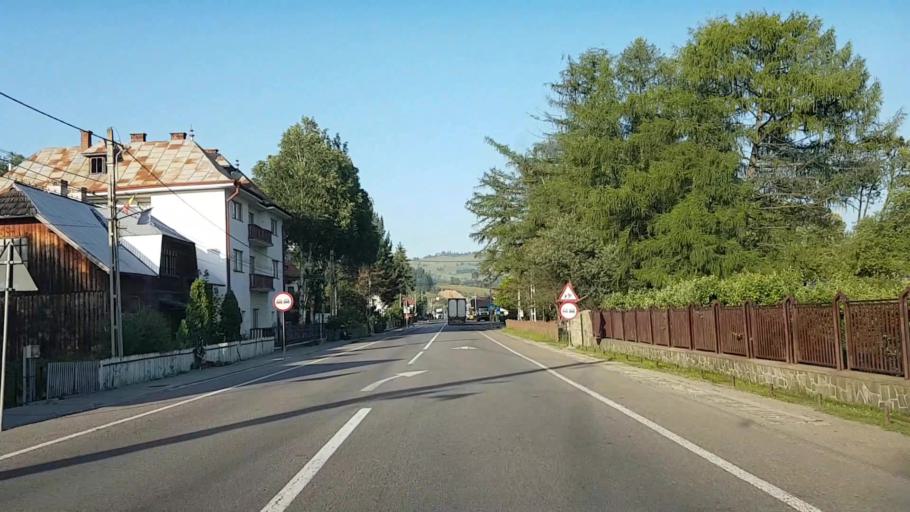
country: RO
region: Suceava
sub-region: Comuna Dorna Candrenilor
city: Dorna Candrenilor
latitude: 47.3549
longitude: 25.2627
